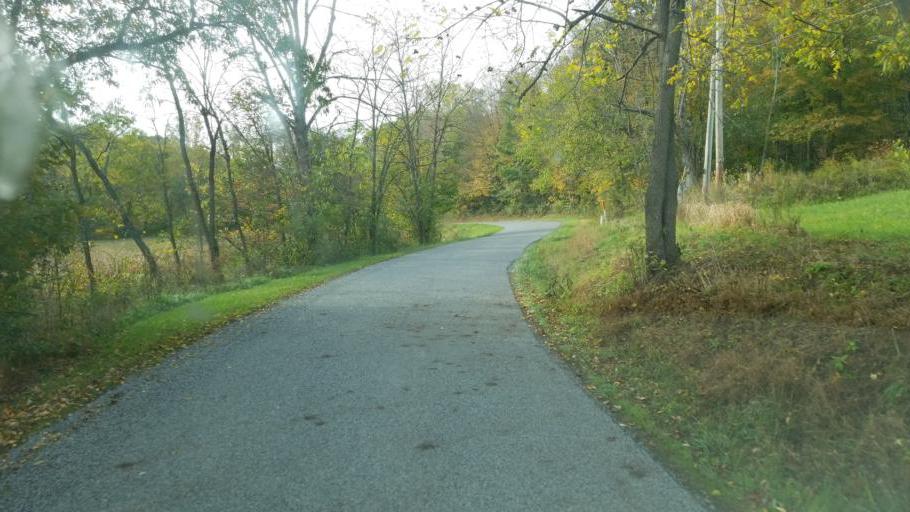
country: US
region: Ohio
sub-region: Holmes County
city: Millersburg
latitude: 40.5354
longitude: -81.8788
